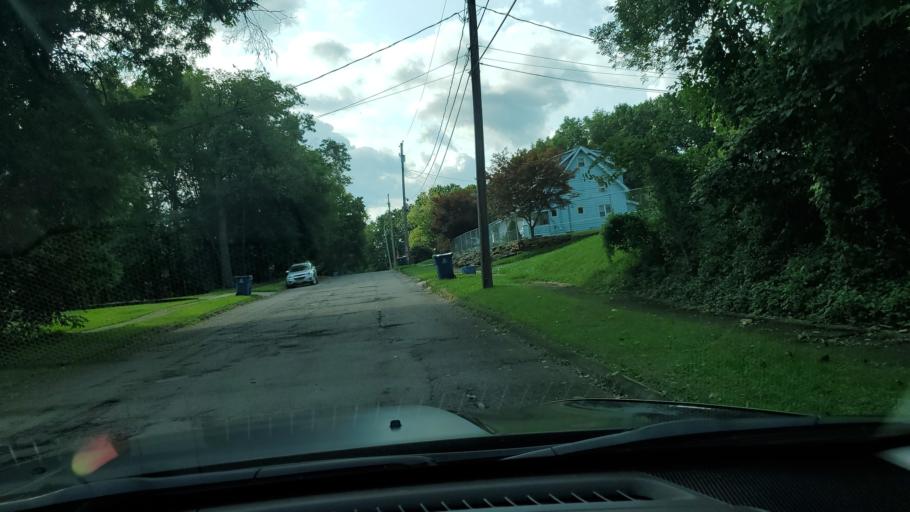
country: US
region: Ohio
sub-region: Mahoning County
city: Struthers
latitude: 41.0524
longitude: -80.5888
